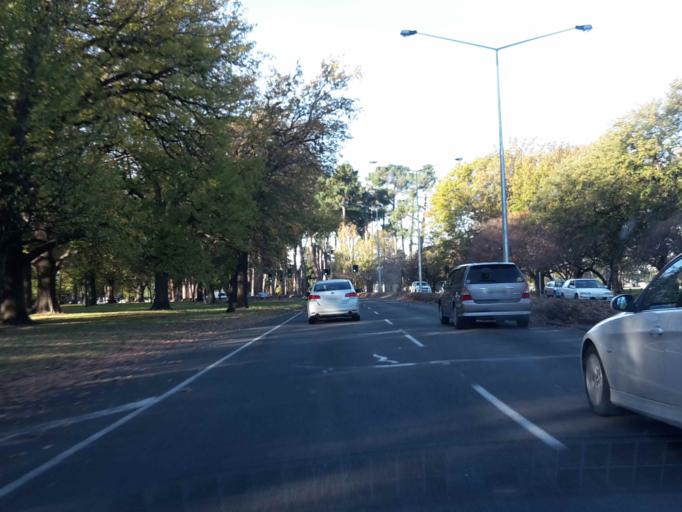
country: NZ
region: Canterbury
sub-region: Christchurch City
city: Christchurch
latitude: -43.5234
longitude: 172.6202
